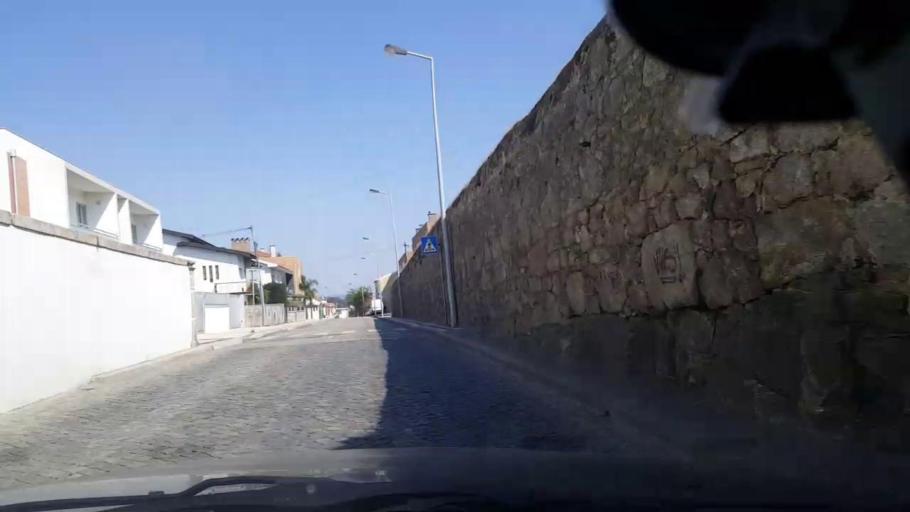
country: PT
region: Porto
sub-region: Vila do Conde
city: Vila do Conde
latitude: 41.3598
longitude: -8.7375
